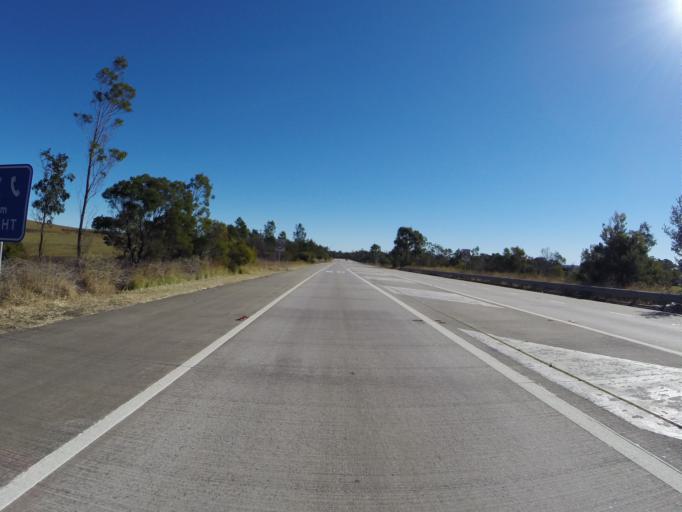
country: AU
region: New South Wales
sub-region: Wollondilly
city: Douglas Park
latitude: -34.2442
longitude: 150.6978
